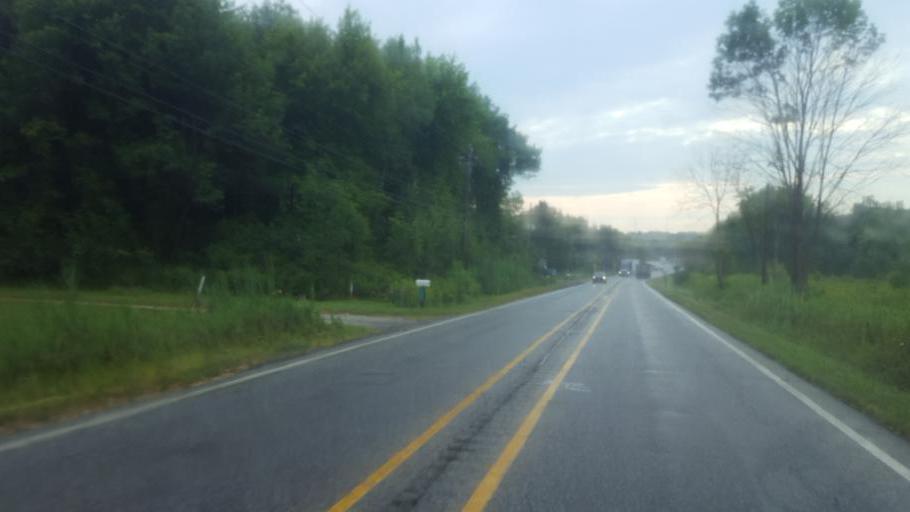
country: US
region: Ohio
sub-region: Portage County
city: Hiram
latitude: 41.3869
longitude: -81.1628
